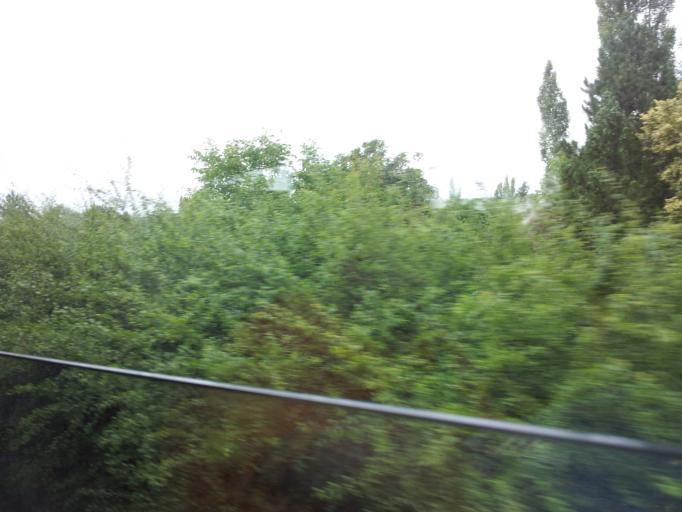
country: HU
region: Veszprem
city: Zanka
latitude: 46.8699
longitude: 17.6834
